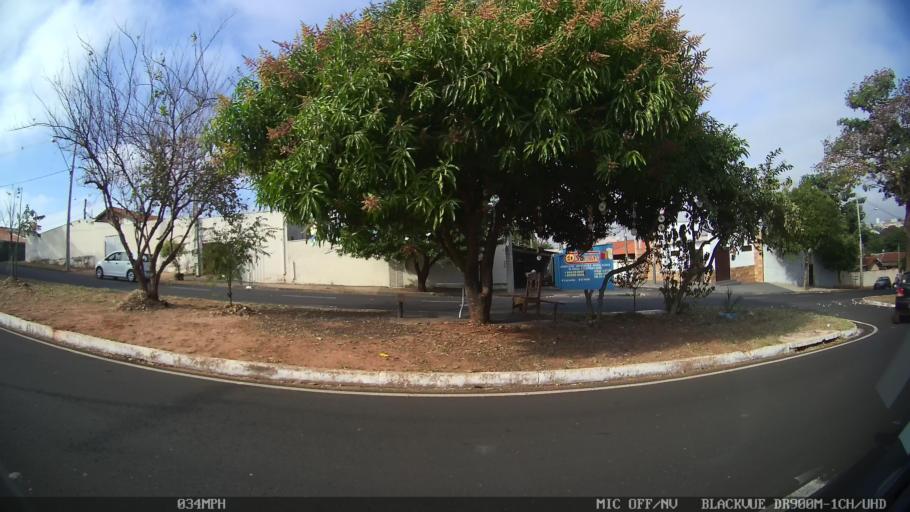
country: BR
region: Sao Paulo
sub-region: Sao Jose Do Rio Preto
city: Sao Jose do Rio Preto
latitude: -20.7943
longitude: -49.4240
